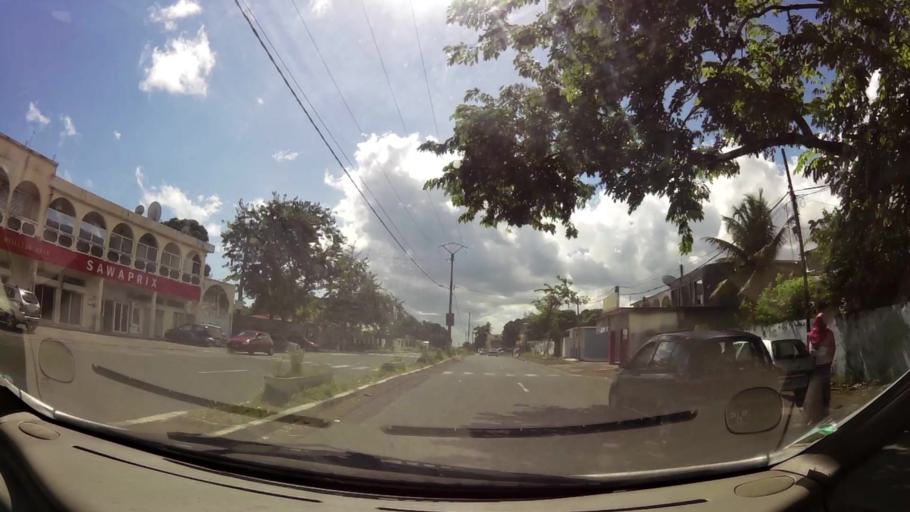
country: KM
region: Grande Comore
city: Mavingouni
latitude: -11.7150
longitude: 43.2459
